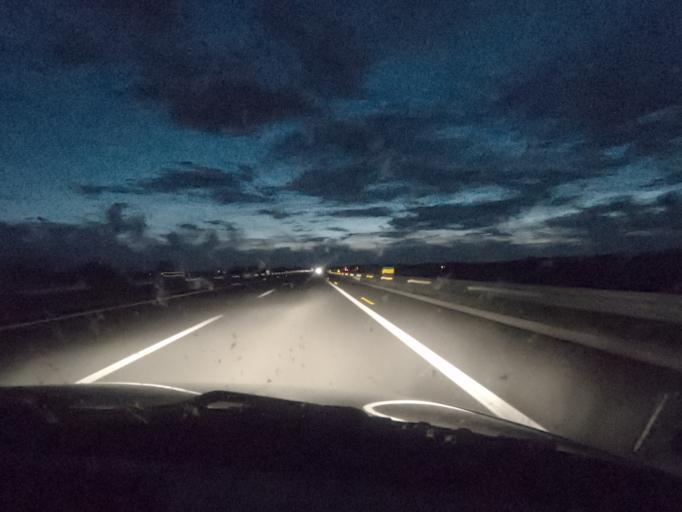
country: ES
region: Extremadura
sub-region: Provincia de Caceres
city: Morcillo
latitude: 39.9741
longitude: -6.3572
